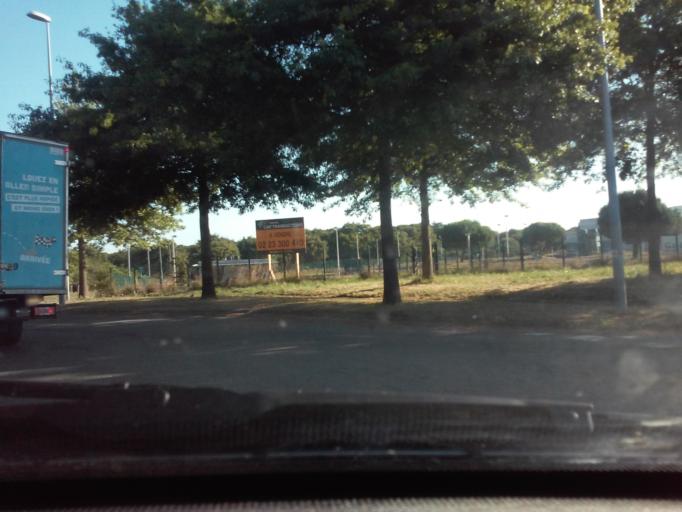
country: FR
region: Pays de la Loire
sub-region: Departement de la Loire-Atlantique
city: Saint-Andre-des-Eaux
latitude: 47.2951
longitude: -2.2880
